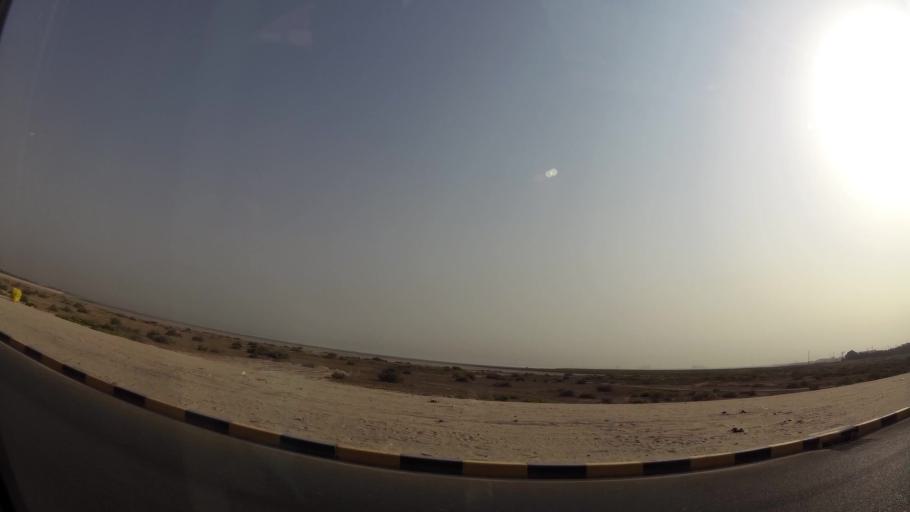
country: KW
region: Al Asimah
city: Ar Rabiyah
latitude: 29.3248
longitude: 47.8189
